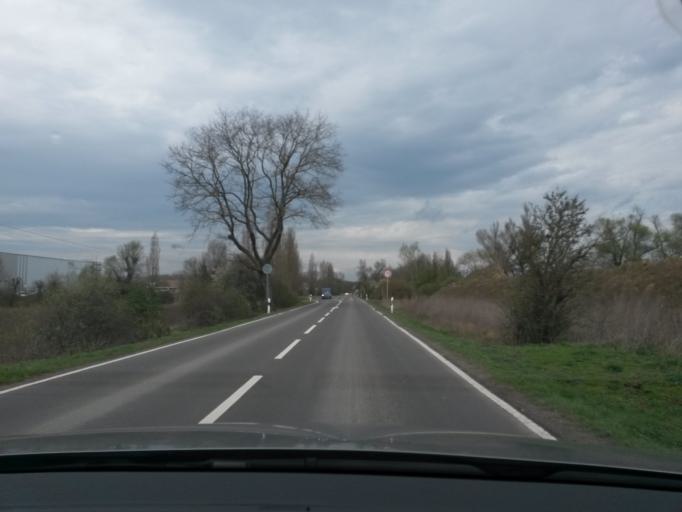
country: DE
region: Rheinland-Pfalz
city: Gimbsheim
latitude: 49.7670
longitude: 8.3832
